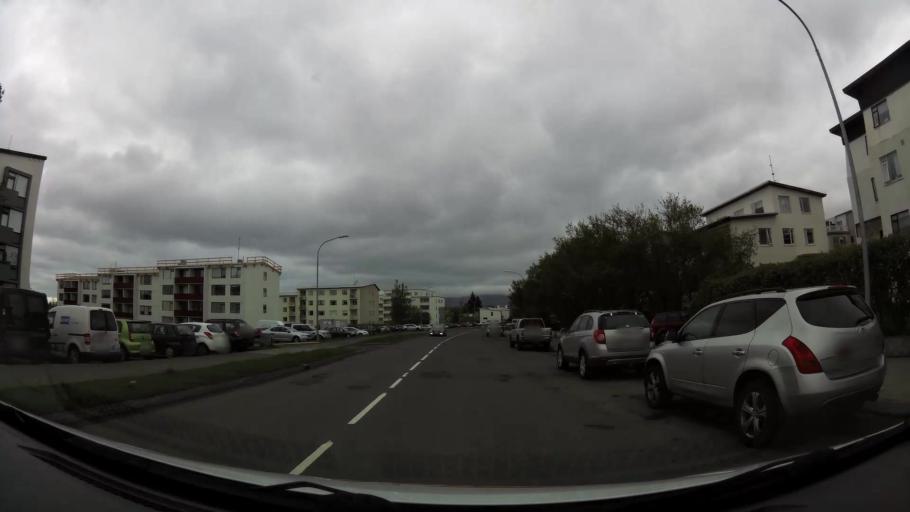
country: IS
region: Capital Region
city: Reykjavik
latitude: 64.1355
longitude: -21.8630
